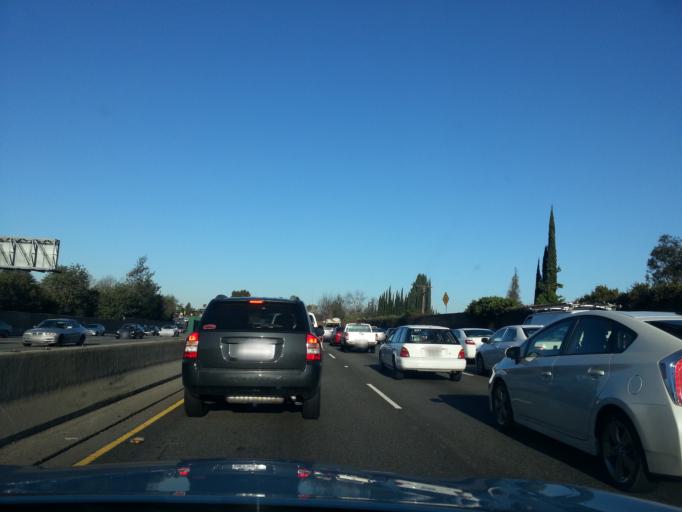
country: US
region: California
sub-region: Los Angeles County
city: Sherman Oaks
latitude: 34.1588
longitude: -118.4581
